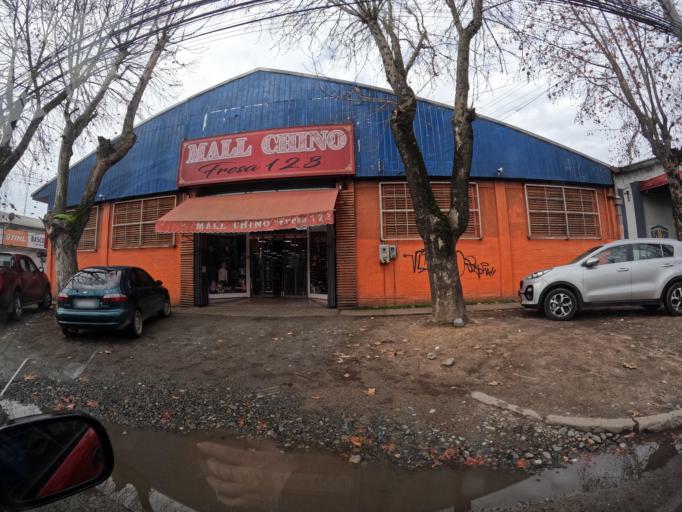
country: CL
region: Maule
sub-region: Provincia de Linares
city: Linares
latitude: -35.8480
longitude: -71.5898
